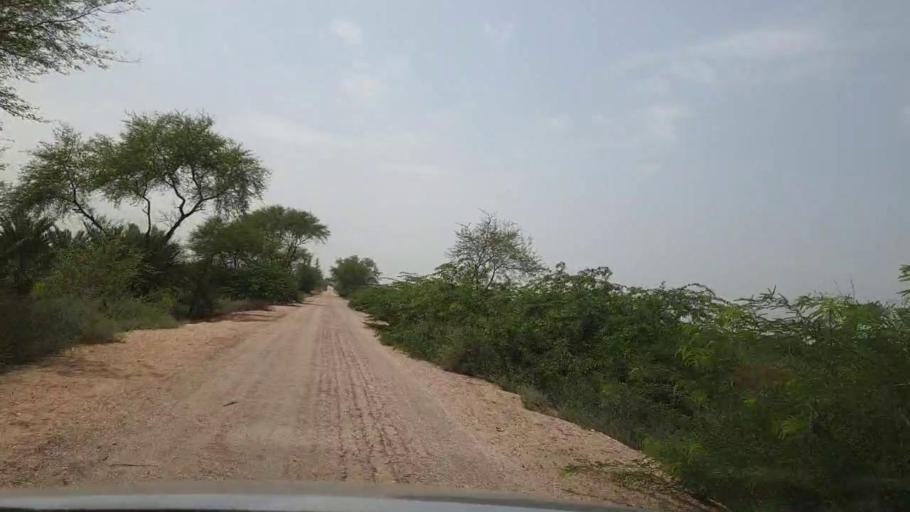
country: PK
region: Sindh
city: Pano Aqil
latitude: 27.5905
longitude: 69.2016
